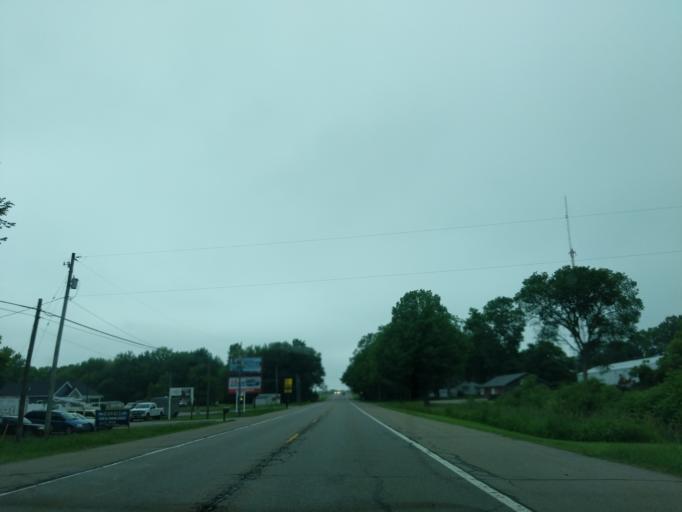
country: US
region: Michigan
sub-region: Branch County
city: Coldwater
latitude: 41.9386
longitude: -84.9484
